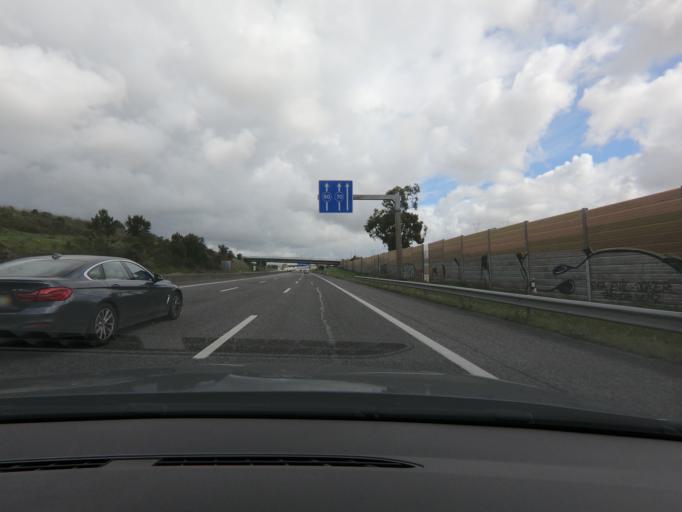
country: PT
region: Lisbon
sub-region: Sintra
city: Queluz
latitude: 38.7603
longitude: -9.2701
